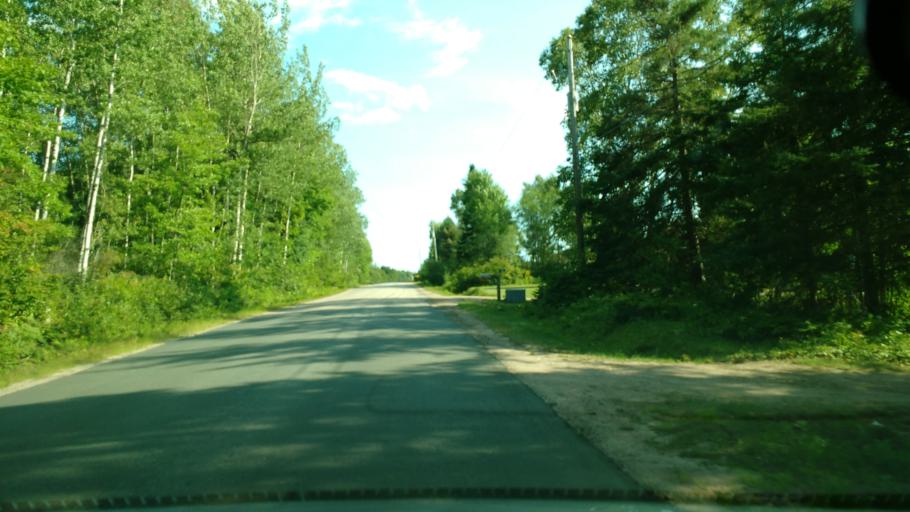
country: CA
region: Ontario
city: Powassan
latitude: 46.1827
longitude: -79.3108
